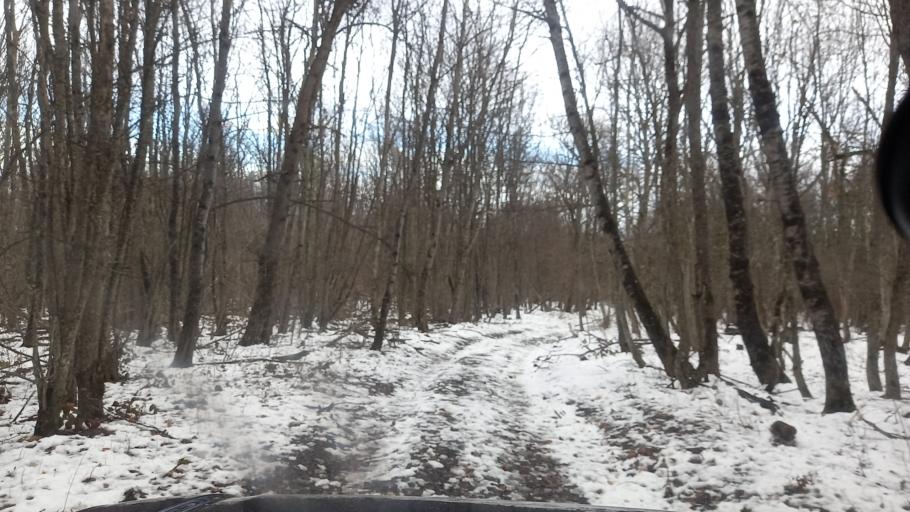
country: RU
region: Adygeya
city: Kamennomostskiy
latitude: 44.2543
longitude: 40.1820
